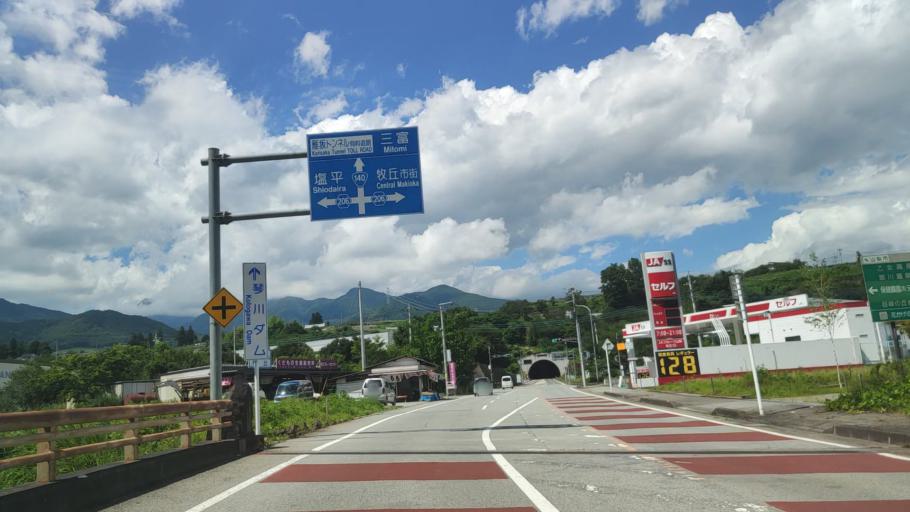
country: JP
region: Yamanashi
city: Enzan
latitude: 35.7414
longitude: 138.7075
